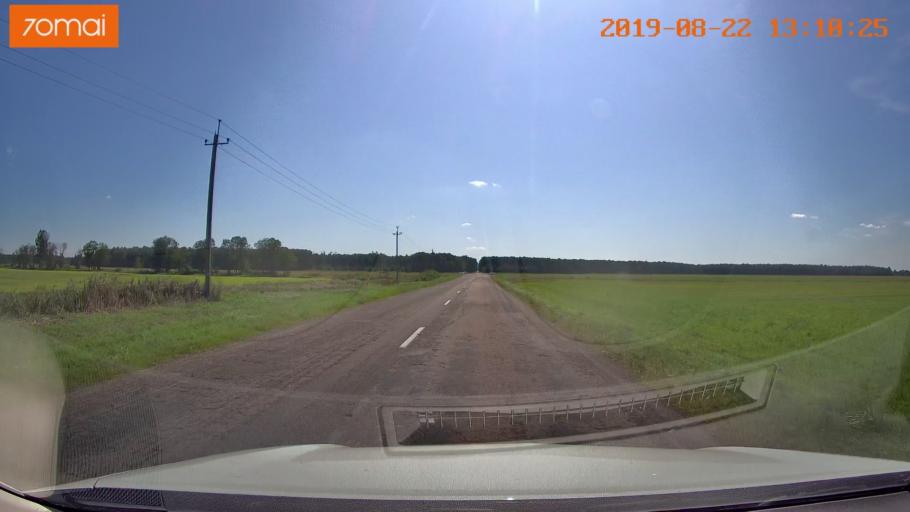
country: BY
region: Minsk
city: Prawdzinski
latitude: 53.2963
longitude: 27.8486
